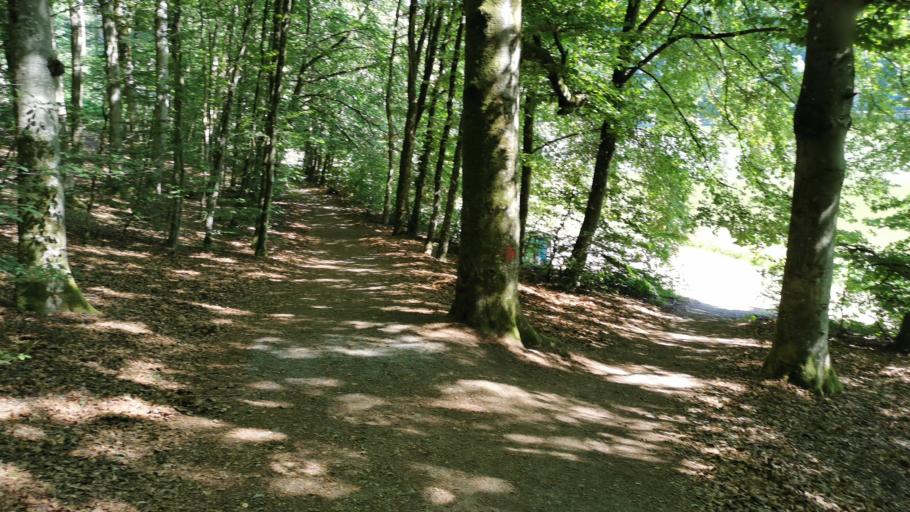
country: DE
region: Rheinland-Pfalz
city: Echtershausen
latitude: 50.0153
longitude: 6.4364
